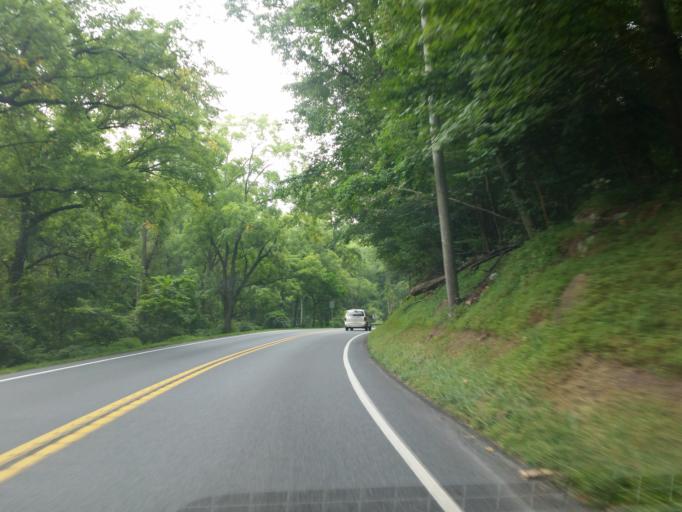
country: US
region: Pennsylvania
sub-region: Lancaster County
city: Brickerville
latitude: 40.2459
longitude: -76.3002
